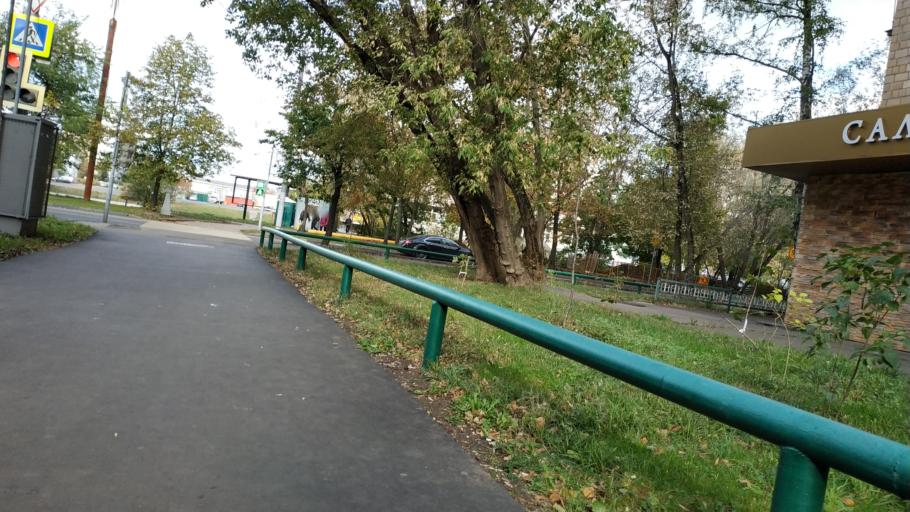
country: RU
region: Moscow
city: Sokol
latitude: 55.8055
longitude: 37.5268
